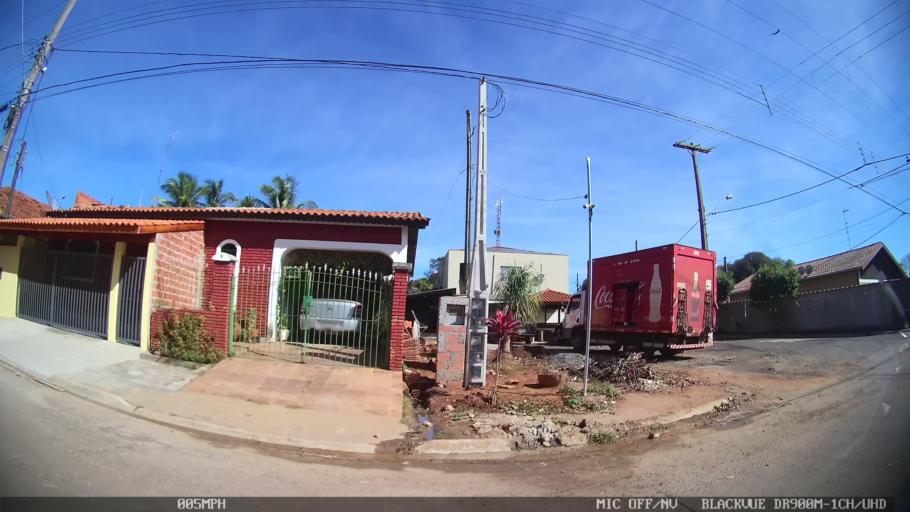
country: BR
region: Sao Paulo
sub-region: Pirassununga
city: Pirassununga
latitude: -22.0779
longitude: -47.4213
